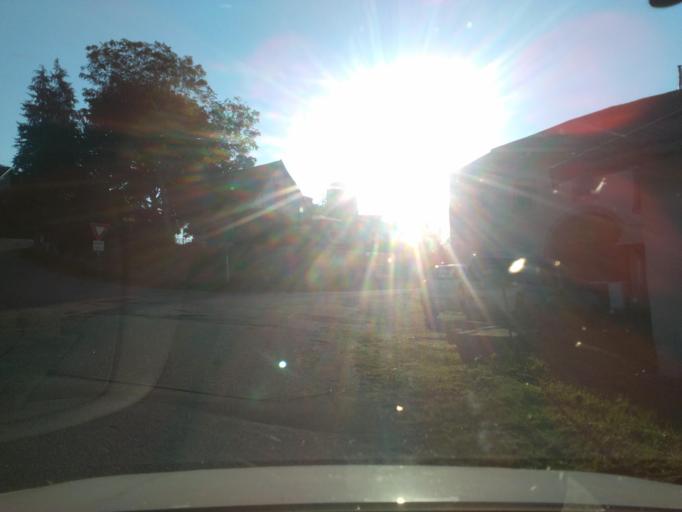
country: FR
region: Lorraine
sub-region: Departement des Vosges
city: Ban-de-Laveline
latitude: 48.3388
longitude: 7.0674
